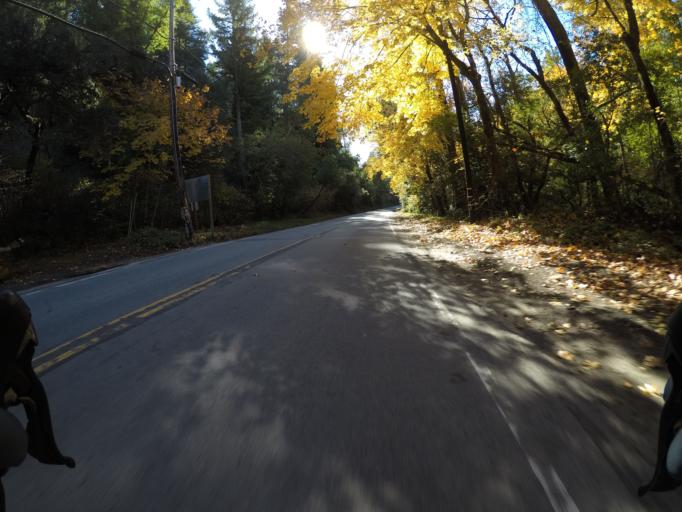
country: US
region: California
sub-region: Santa Cruz County
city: Lompico
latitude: 37.0810
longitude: -122.0506
